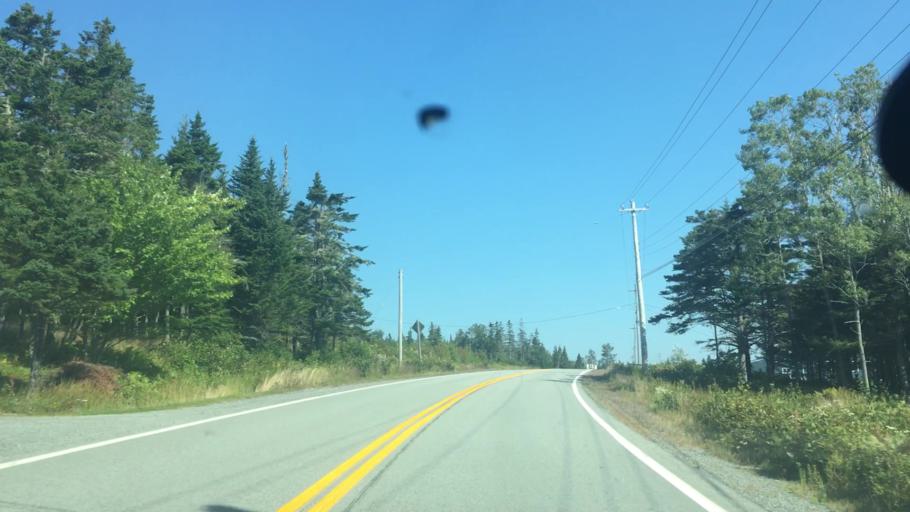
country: CA
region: Nova Scotia
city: New Glasgow
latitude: 44.9281
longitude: -62.2981
